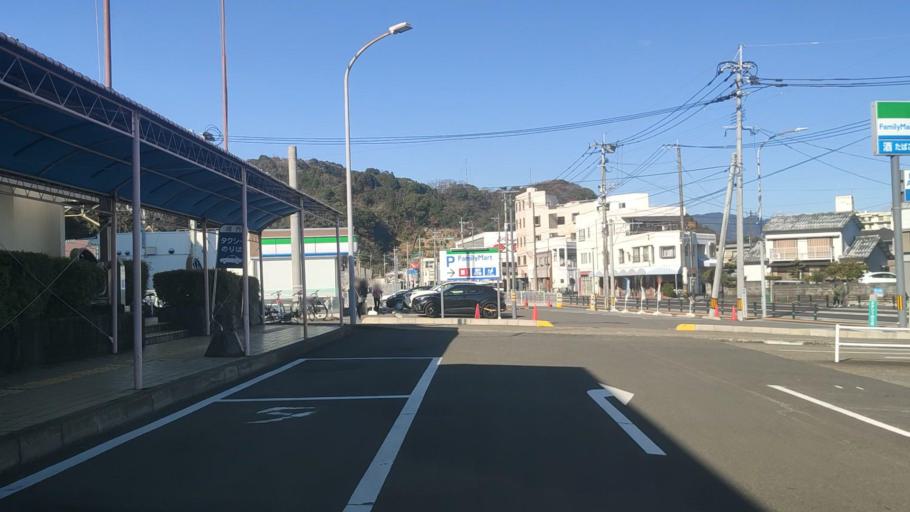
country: JP
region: Oita
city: Saiki
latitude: 32.9725
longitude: 131.9022
